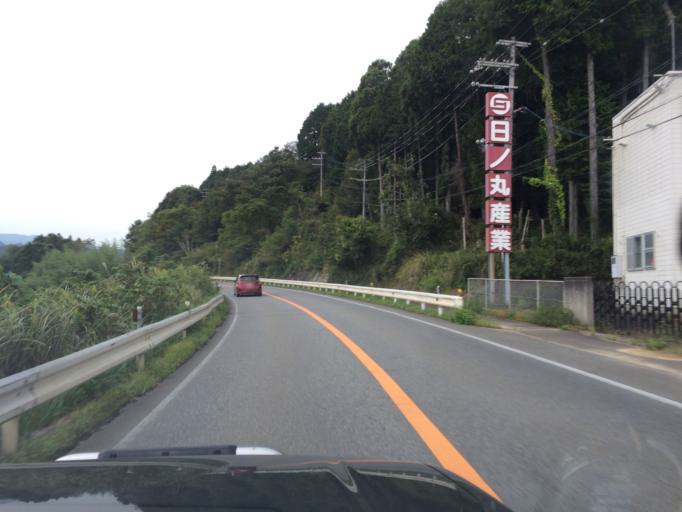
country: JP
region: Hyogo
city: Toyooka
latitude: 35.3884
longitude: 134.8137
